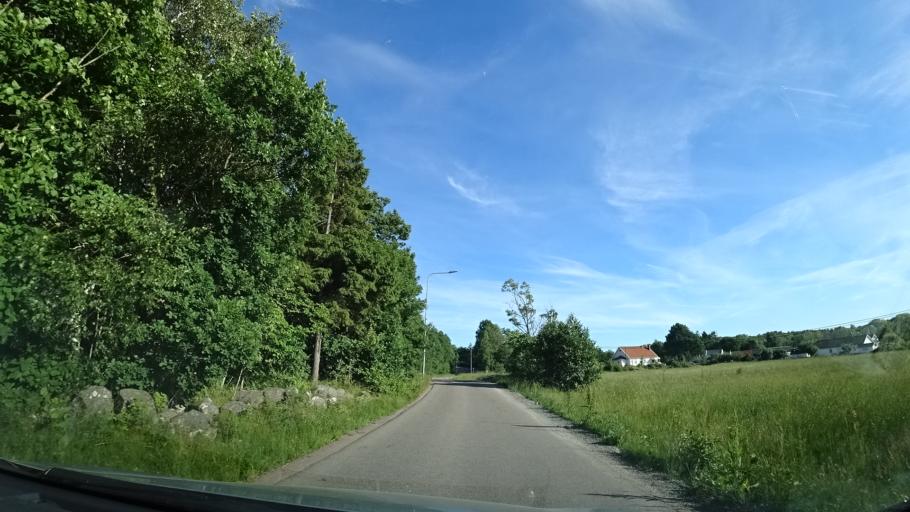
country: SE
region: Vaestra Goetaland
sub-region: Goteborg
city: Billdal
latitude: 57.5781
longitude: 11.9625
